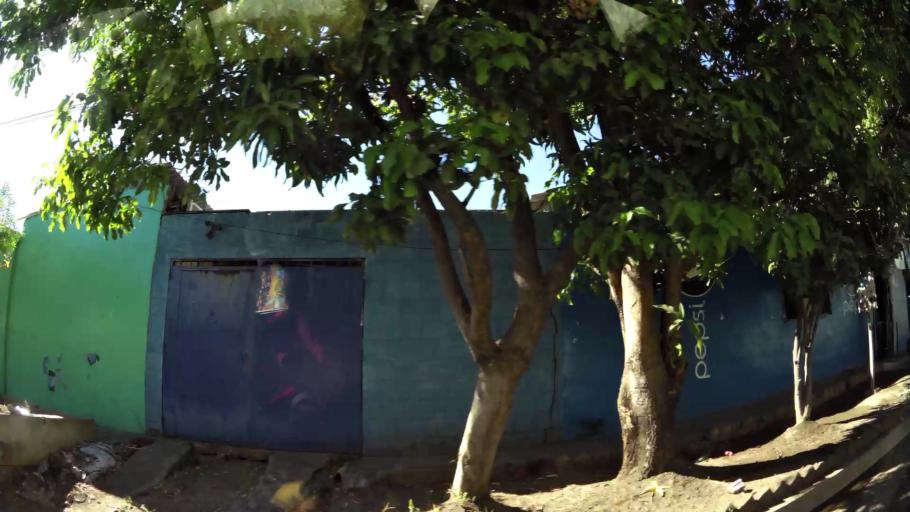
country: SV
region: San Miguel
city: San Miguel
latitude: 13.4709
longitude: -88.1537
